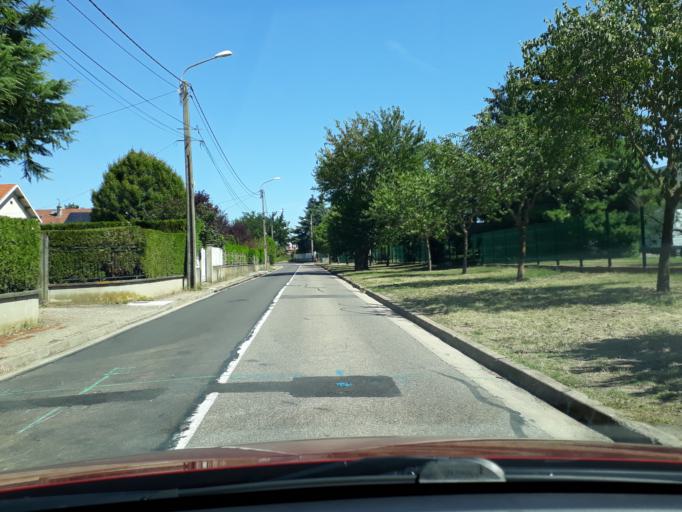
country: FR
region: Rhone-Alpes
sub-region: Departement du Rhone
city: Genas
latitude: 45.7024
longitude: 4.9830
